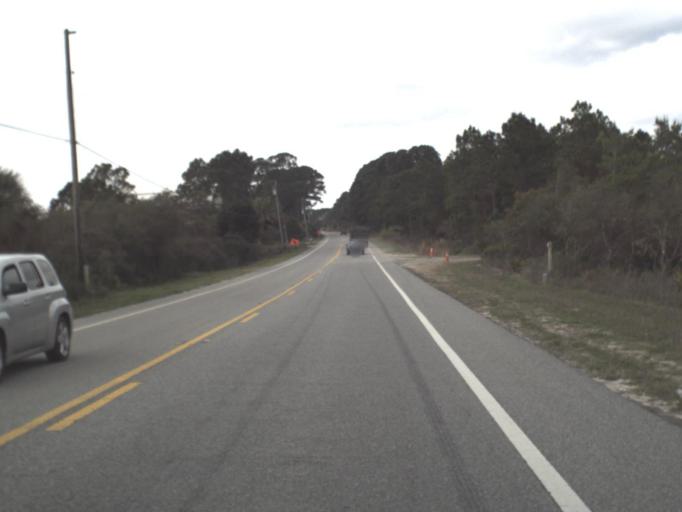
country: US
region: Florida
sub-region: Franklin County
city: Carrabelle
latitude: 29.7999
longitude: -84.7426
